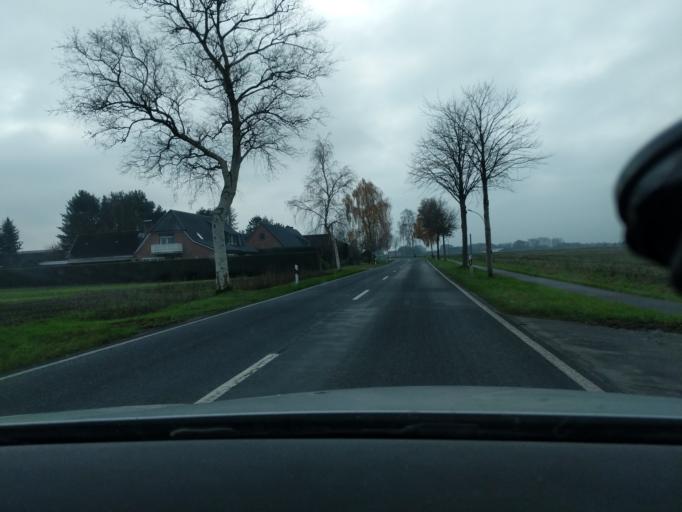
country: DE
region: Lower Saxony
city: Ahlerstedt
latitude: 53.3893
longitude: 9.4801
